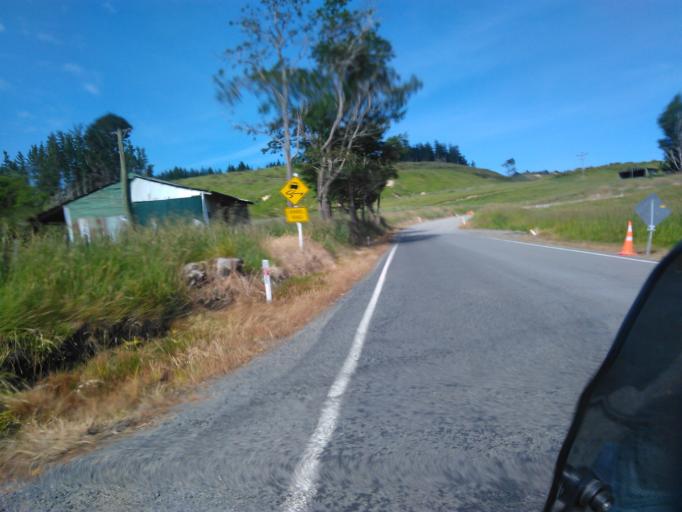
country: NZ
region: Hawke's Bay
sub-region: Wairoa District
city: Wairoa
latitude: -38.8714
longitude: 177.2112
